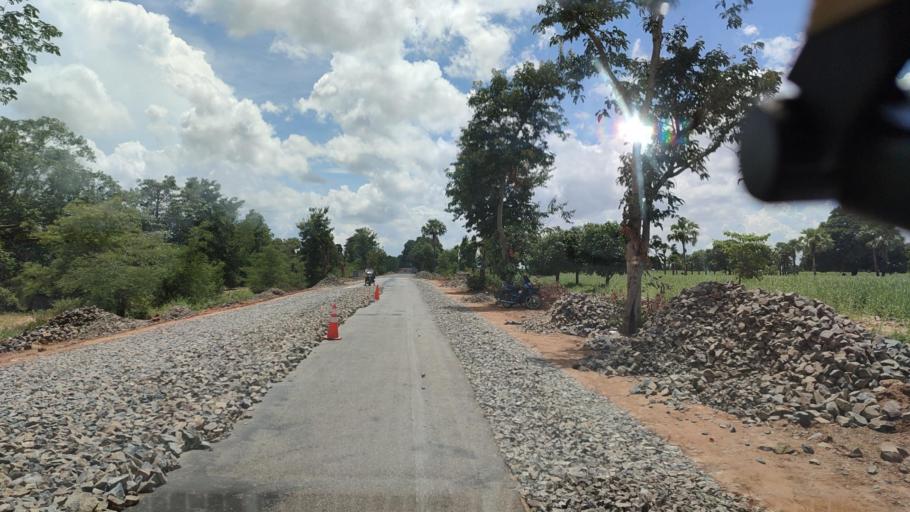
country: MM
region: Magway
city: Magway
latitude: 20.1950
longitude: 95.0753
